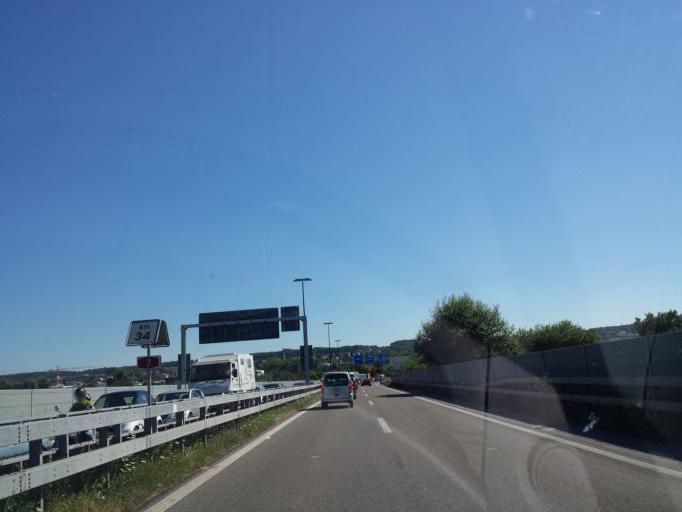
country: DE
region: Baden-Wuerttemberg
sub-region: Freiburg Region
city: Konstanz
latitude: 47.6608
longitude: 9.1612
